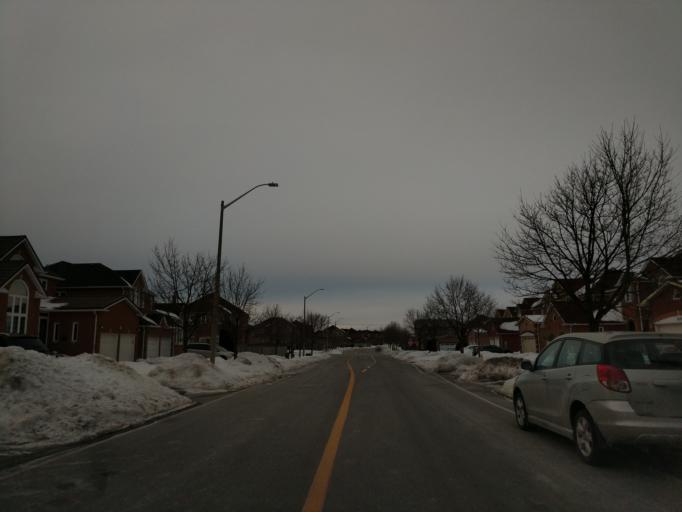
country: CA
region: Ontario
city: Markham
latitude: 43.8463
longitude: -79.2747
